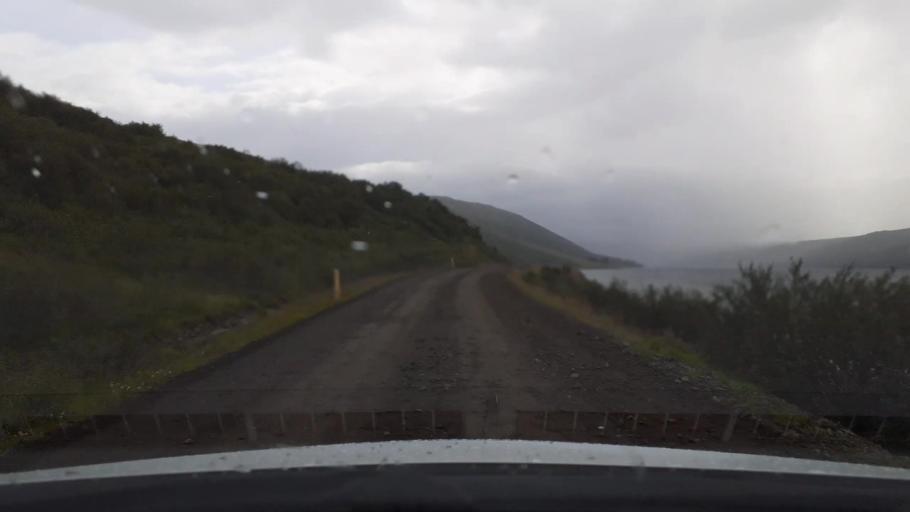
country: IS
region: Capital Region
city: Mosfellsbaer
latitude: 64.5114
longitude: -21.3998
